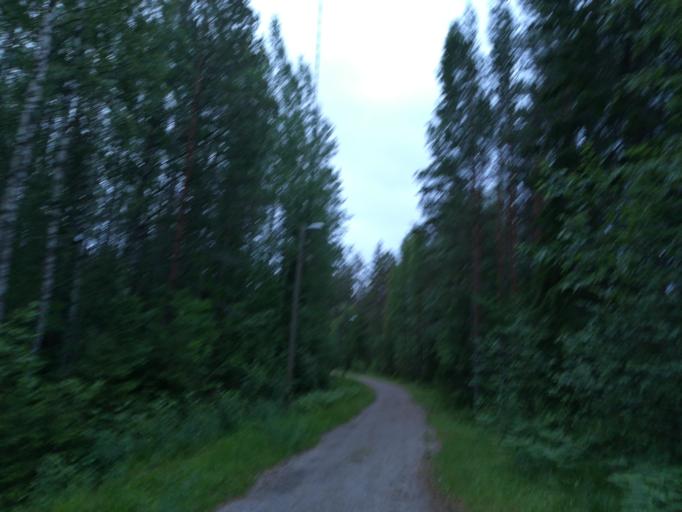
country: FI
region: Southern Savonia
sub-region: Mikkeli
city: Ristiina
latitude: 61.4864
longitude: 27.2802
